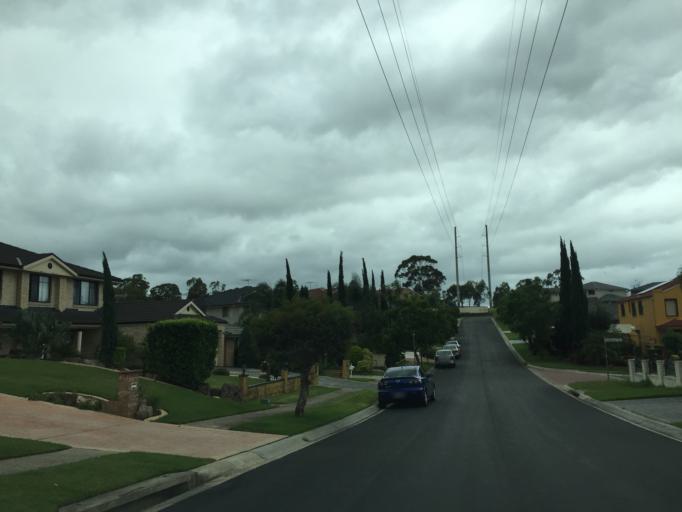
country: AU
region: New South Wales
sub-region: Blacktown
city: Blacktown
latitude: -33.7927
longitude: 150.9002
